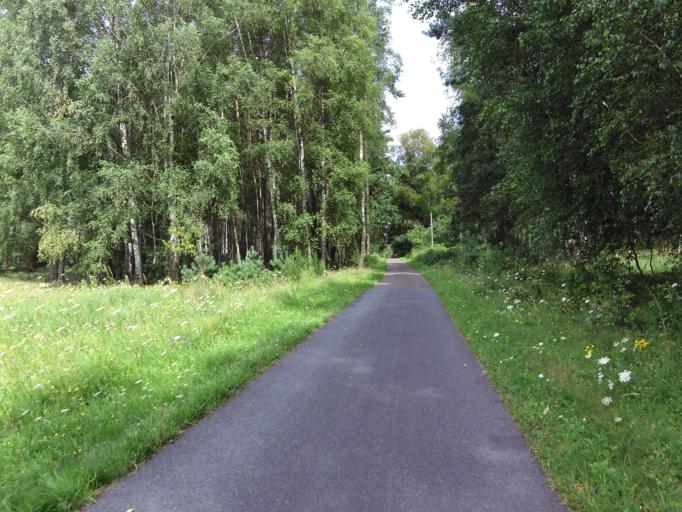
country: DE
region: Brandenburg
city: Lychen
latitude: 53.2622
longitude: 13.3080
